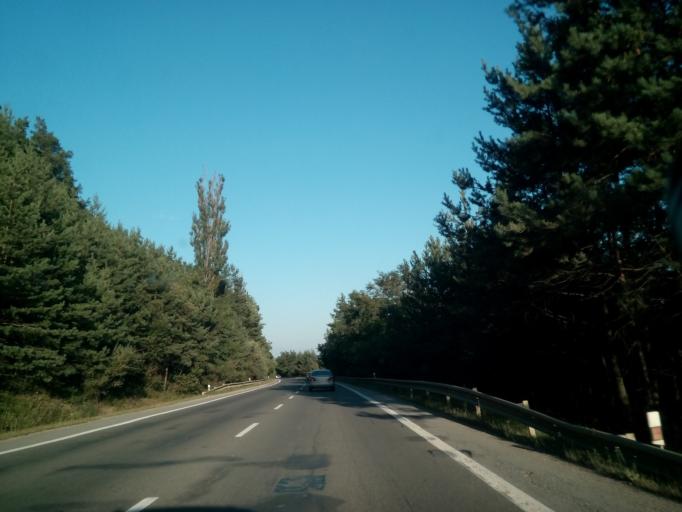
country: SK
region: Presovsky
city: Sabinov
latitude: 49.0118
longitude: 21.0521
